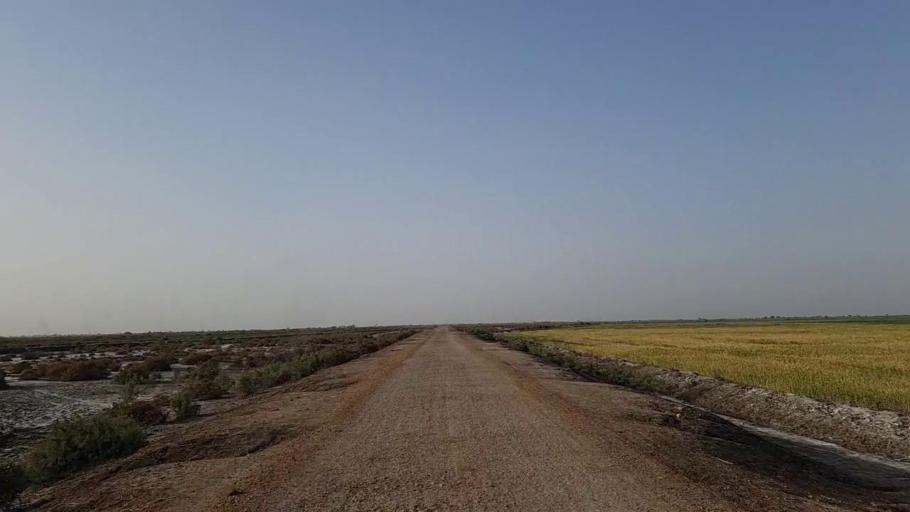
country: PK
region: Sindh
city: Jati
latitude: 24.3516
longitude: 68.1494
